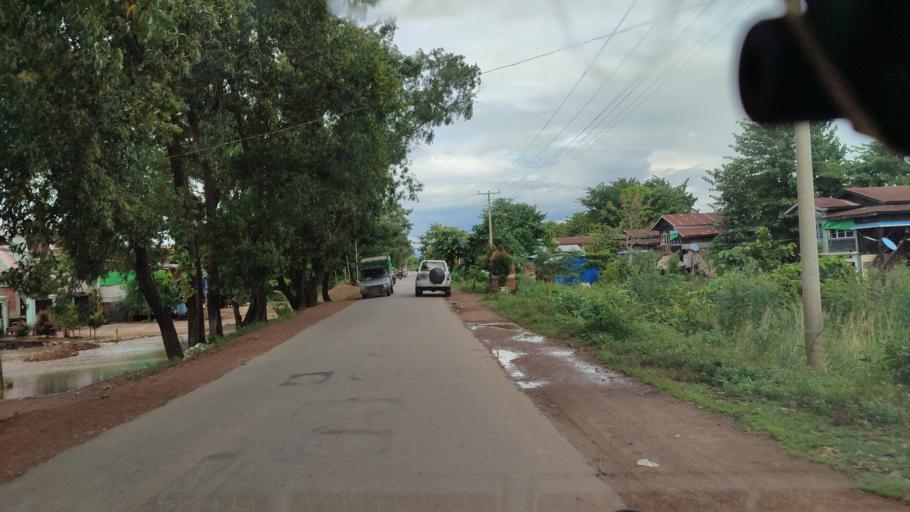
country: MM
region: Bago
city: Nyaunglebin
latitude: 17.9186
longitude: 96.8533
